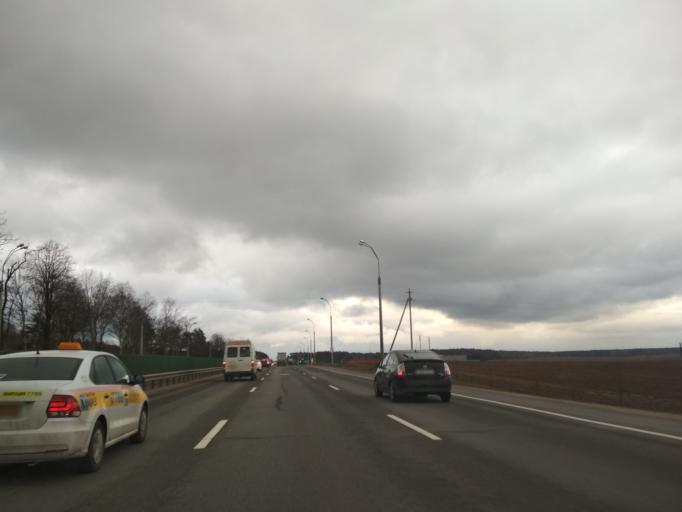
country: BY
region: Minsk
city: Vyaliki Trastsyanets
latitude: 53.8361
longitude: 27.7300
